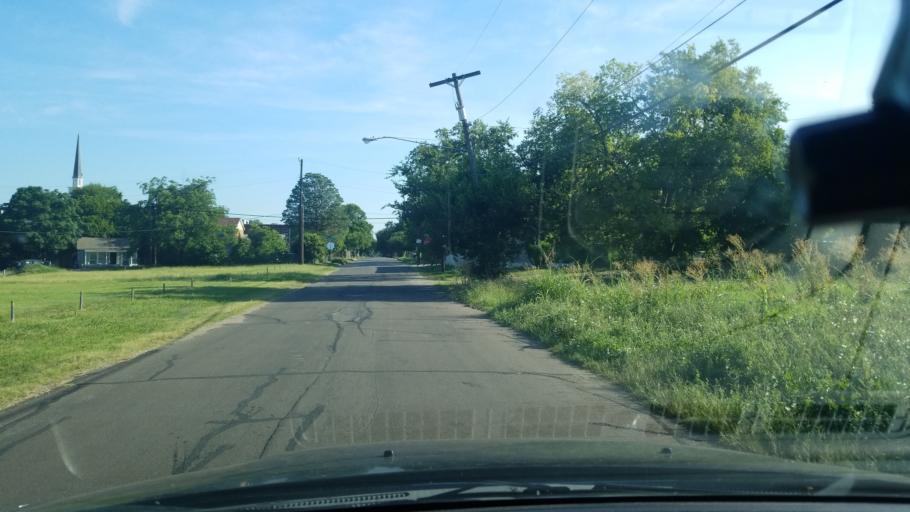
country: US
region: Texas
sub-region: Dallas County
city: Dallas
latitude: 32.7142
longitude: -96.8121
